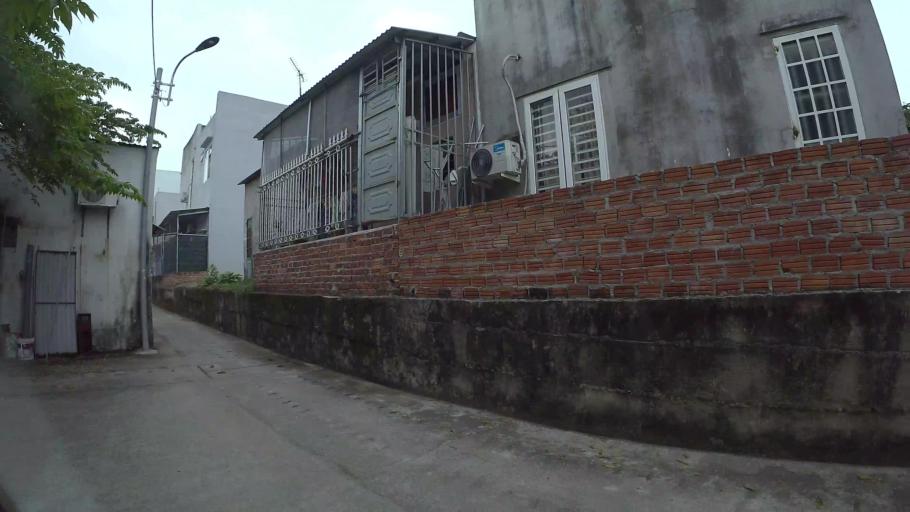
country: VN
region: Da Nang
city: Lien Chieu
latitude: 16.0515
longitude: 108.1584
